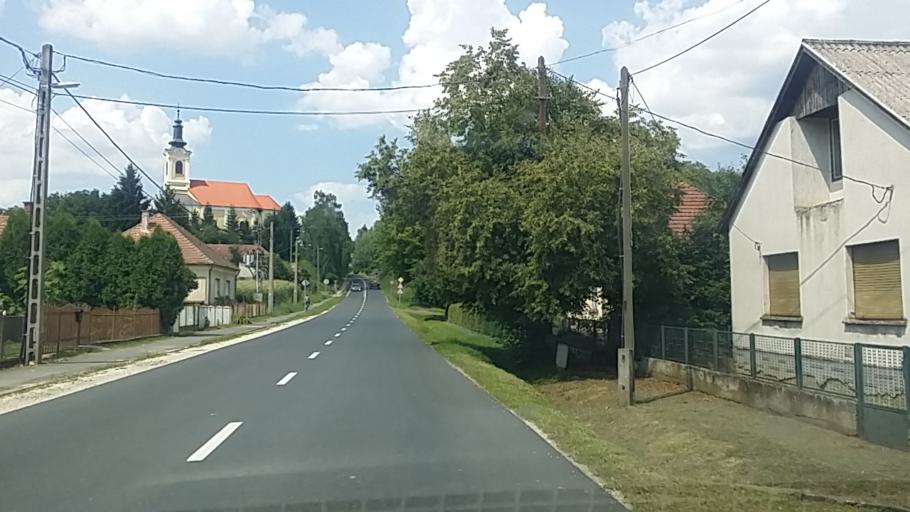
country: HR
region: Medimurska
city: Podturen
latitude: 46.5188
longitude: 16.5565
